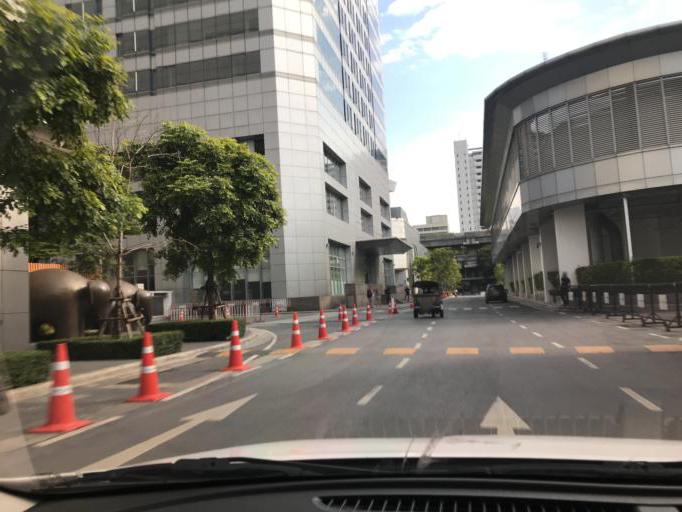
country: TH
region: Bangkok
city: Ratchathewi
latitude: 13.7466
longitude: 100.5381
